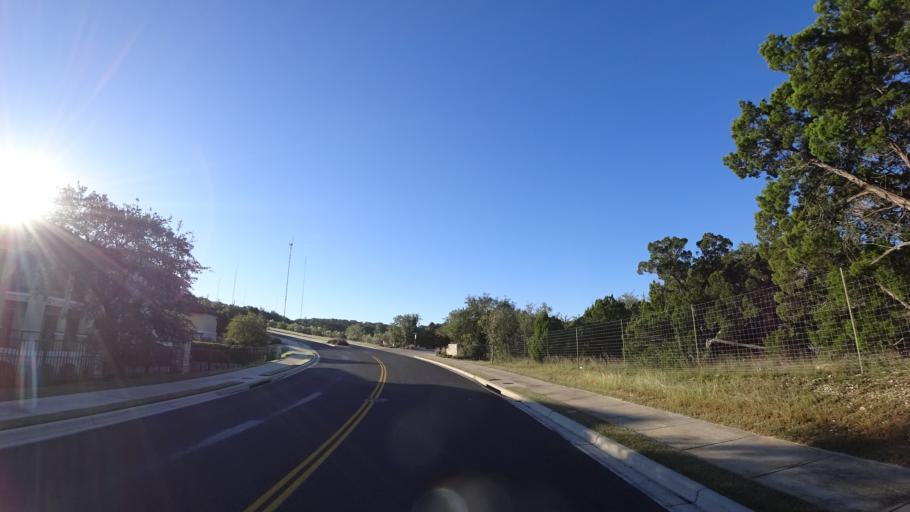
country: US
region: Texas
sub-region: Travis County
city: West Lake Hills
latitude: 30.3322
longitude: -97.8116
